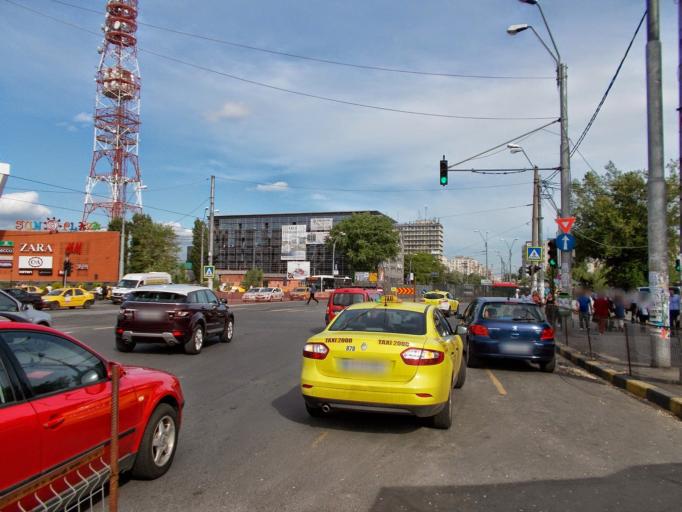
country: RO
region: Bucuresti
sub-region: Municipiul Bucuresti
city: Bucharest
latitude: 44.3937
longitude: 26.1207
